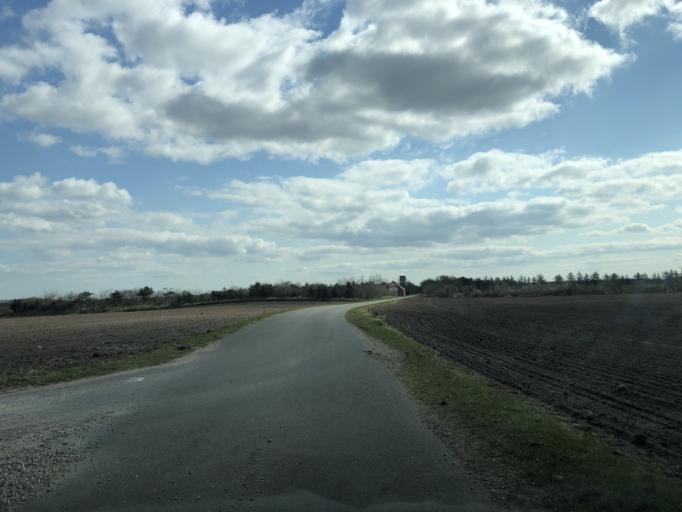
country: DK
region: Central Jutland
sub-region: Holstebro Kommune
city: Ulfborg
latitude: 56.4005
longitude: 8.2145
